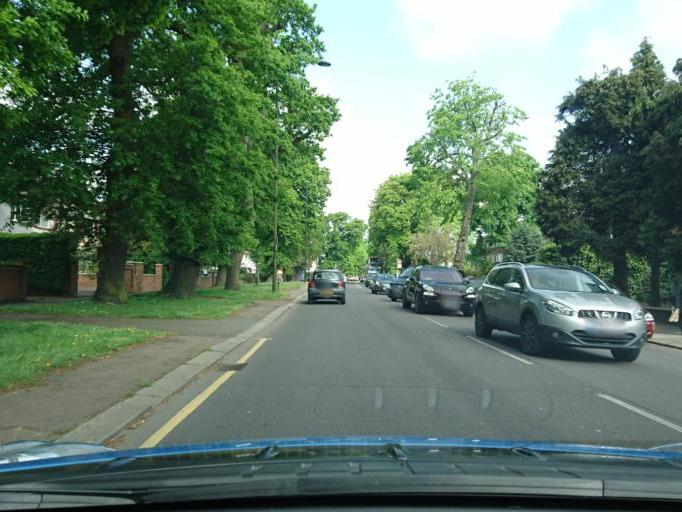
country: GB
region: England
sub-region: Greater London
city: Wood Green
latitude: 51.6357
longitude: -0.1365
